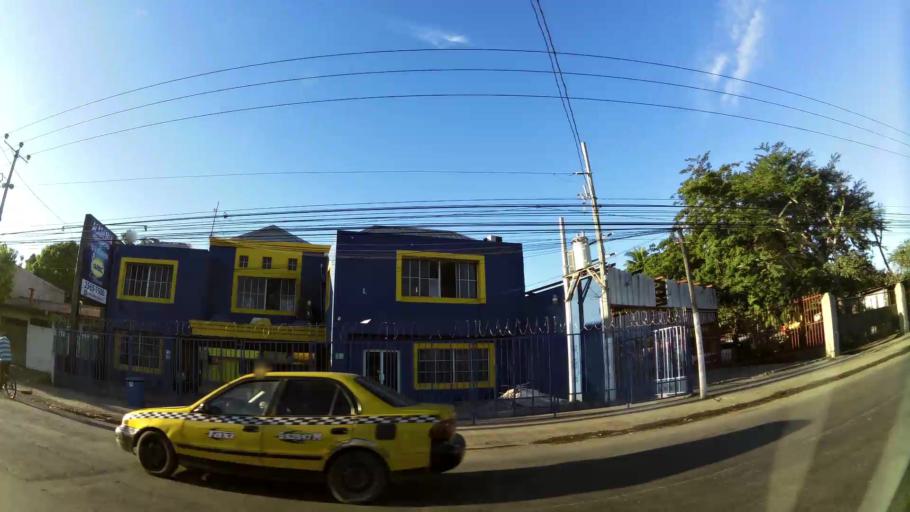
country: SV
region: San Miguel
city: San Miguel
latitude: 13.4677
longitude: -88.1768
